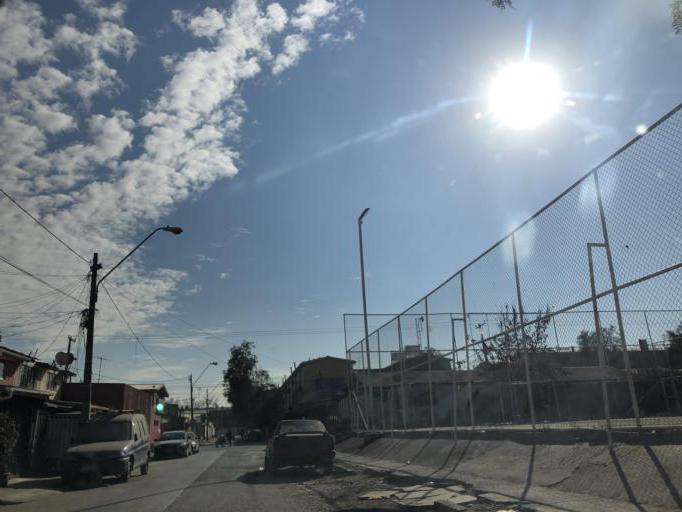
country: CL
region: Santiago Metropolitan
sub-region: Provincia de Santiago
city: La Pintana
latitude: -33.6268
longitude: -70.6213
